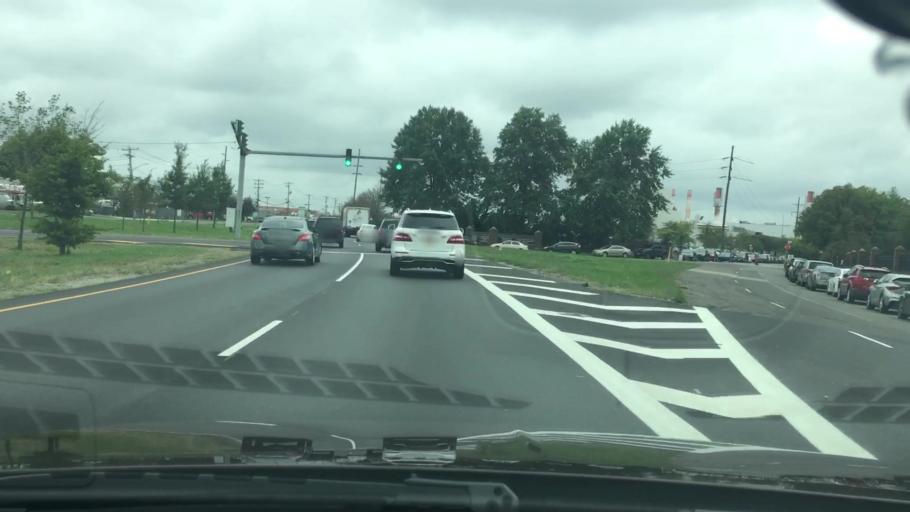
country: US
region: New York
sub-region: Nassau County
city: Bethpage
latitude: 40.7431
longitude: -73.4970
